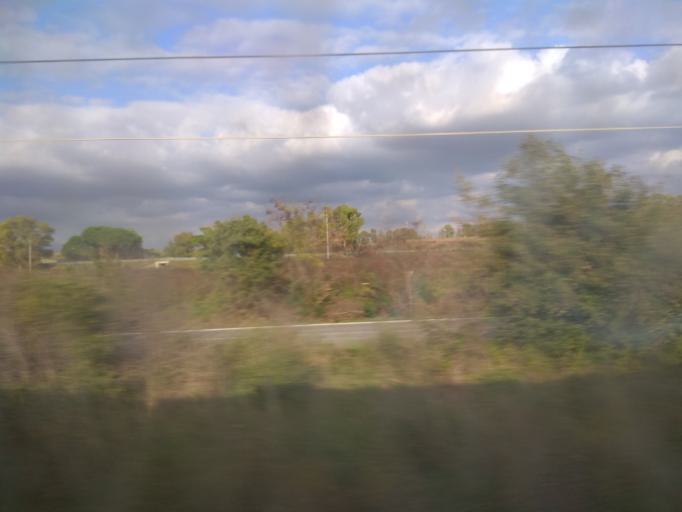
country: IT
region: Latium
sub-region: Citta metropolitana di Roma Capitale
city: Maccarese
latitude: 41.9087
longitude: 12.2076
